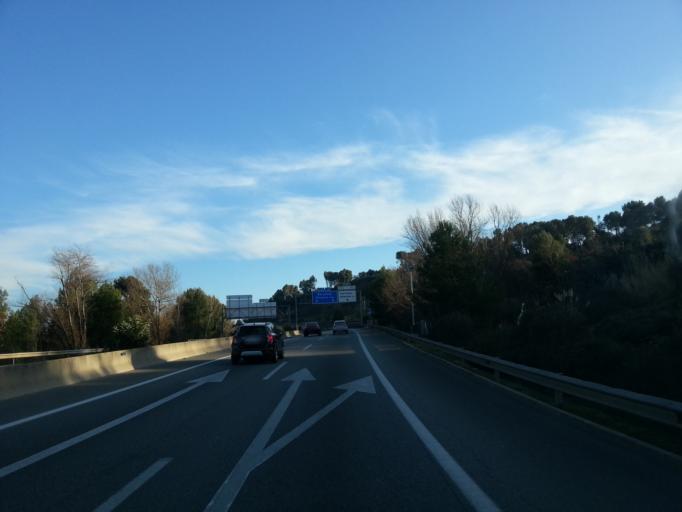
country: ES
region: Catalonia
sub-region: Provincia de Barcelona
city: Terrassa
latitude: 41.5535
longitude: 1.9985
